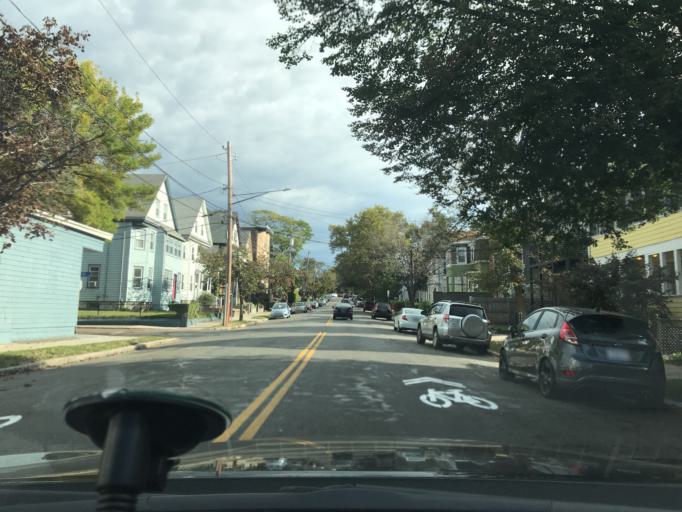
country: US
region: Massachusetts
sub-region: Middlesex County
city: Medford
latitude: 42.3992
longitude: -71.1282
